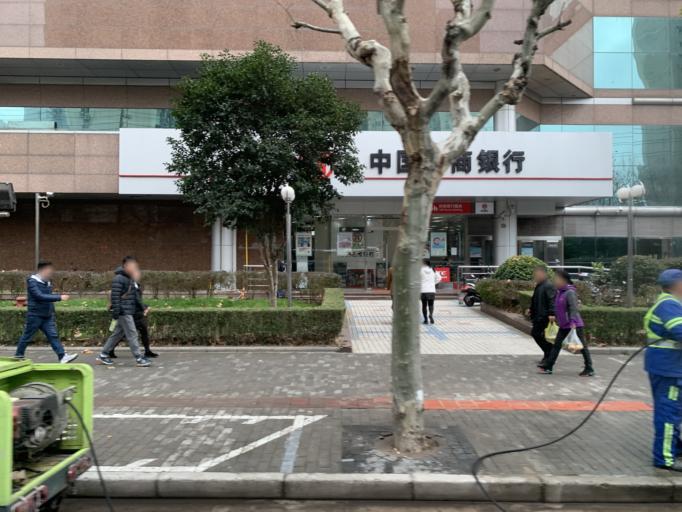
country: CN
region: Shanghai Shi
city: Pudong
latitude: 31.2285
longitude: 121.5192
